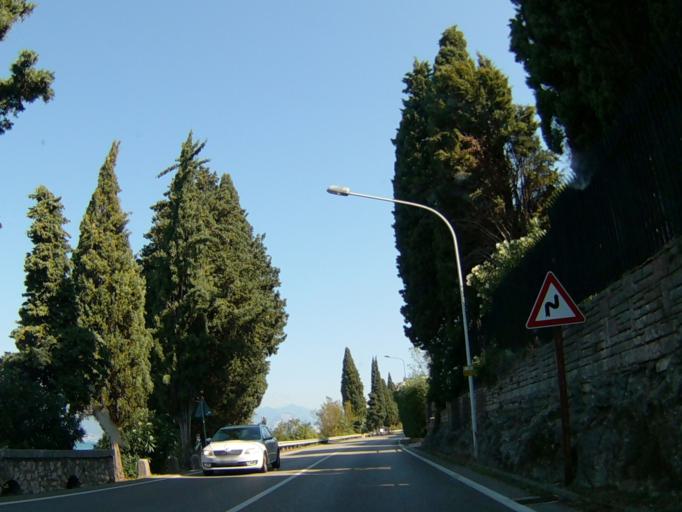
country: IT
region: Veneto
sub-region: Provincia di Verona
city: Torri del Benaco
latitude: 45.5907
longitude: 10.6777
